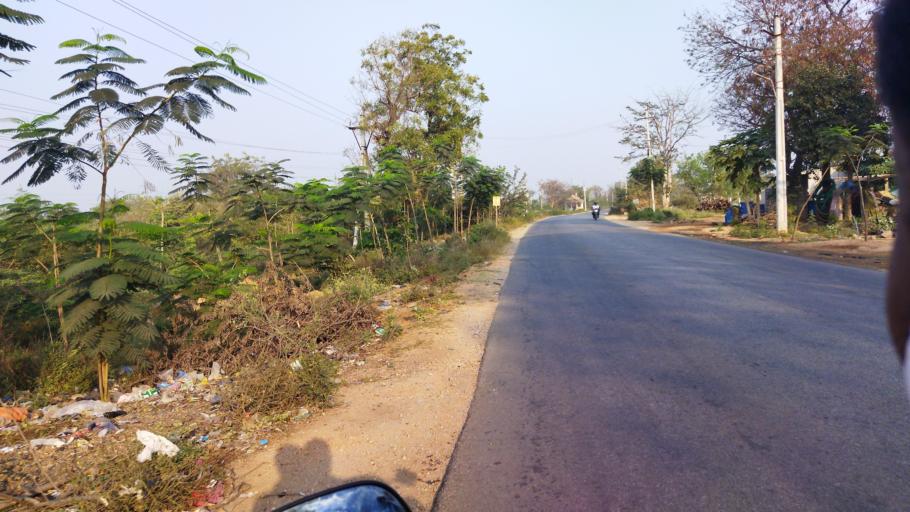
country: IN
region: Telangana
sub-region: Nalgonda
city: Nalgonda
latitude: 17.2406
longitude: 79.1158
